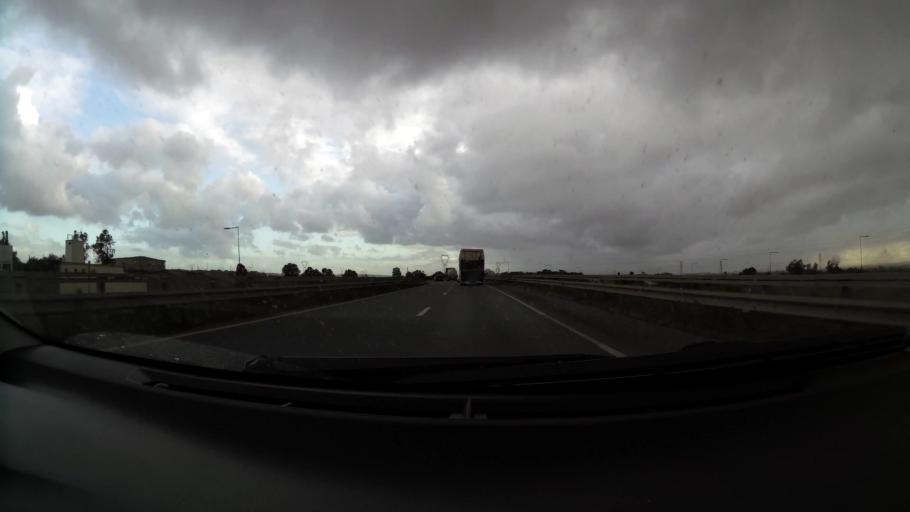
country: MA
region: Grand Casablanca
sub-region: Mohammedia
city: Mohammedia
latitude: 33.6493
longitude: -7.4188
